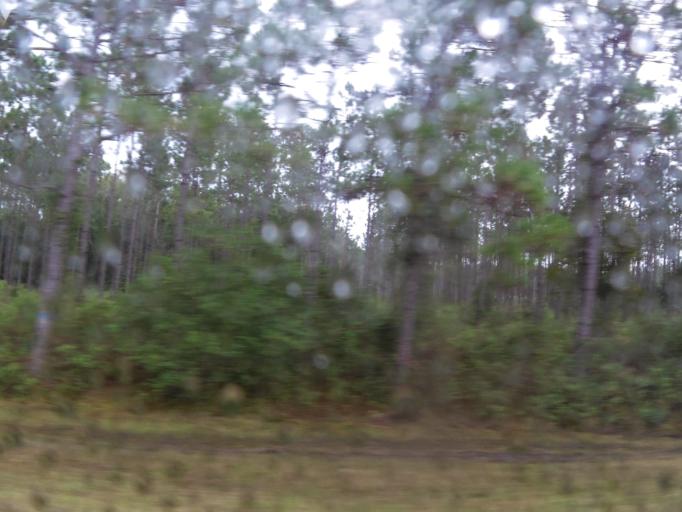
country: US
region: Florida
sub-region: Baker County
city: Macclenny
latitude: 30.3965
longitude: -82.1207
